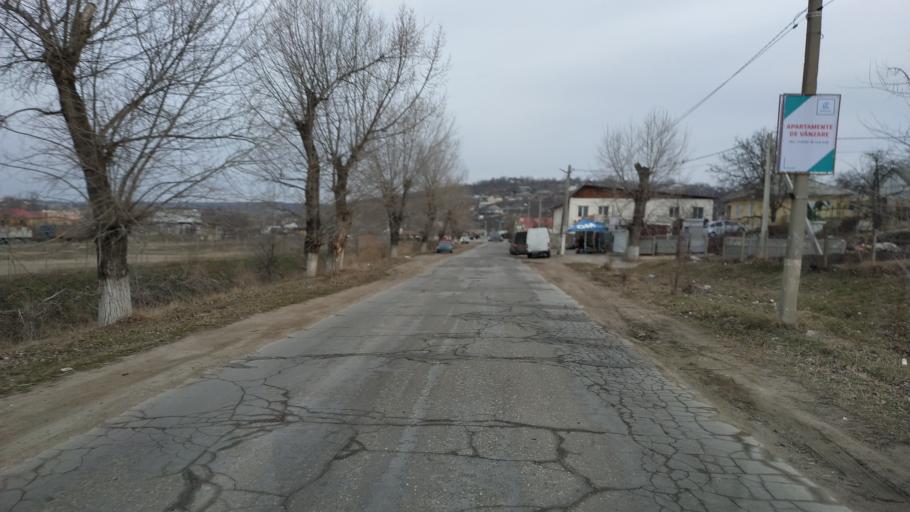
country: MD
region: Chisinau
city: Vatra
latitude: 47.0859
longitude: 28.7708
